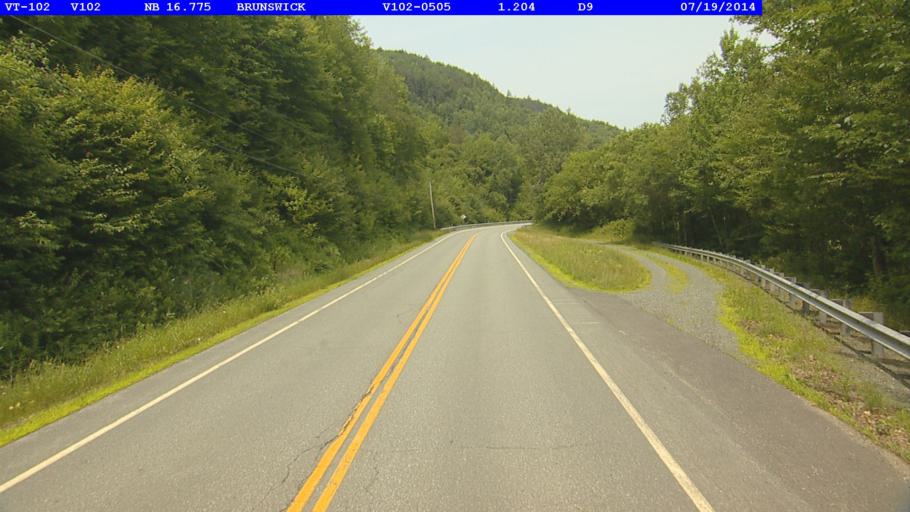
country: US
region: New Hampshire
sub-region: Coos County
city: Stratford
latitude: 44.6777
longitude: -71.5971
